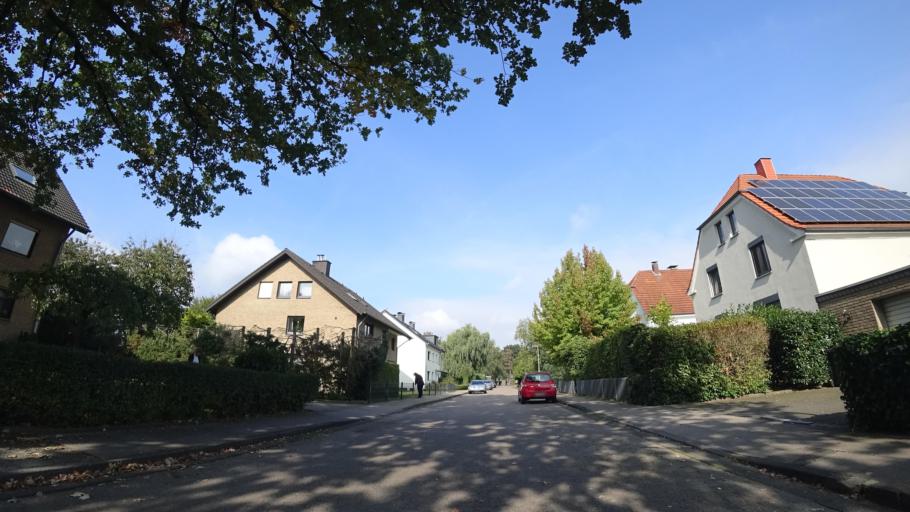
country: DE
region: North Rhine-Westphalia
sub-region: Regierungsbezirk Detmold
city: Bielefeld
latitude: 52.0544
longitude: 8.5394
